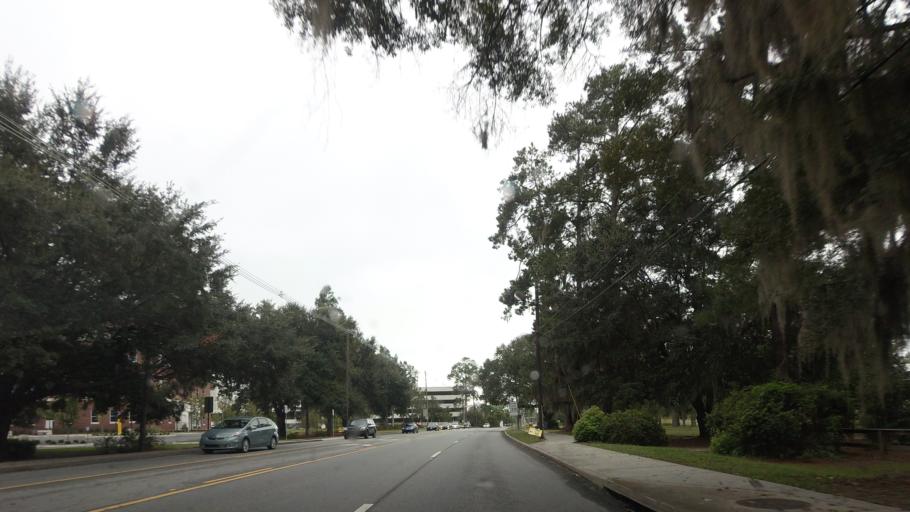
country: US
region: Georgia
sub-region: Lowndes County
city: Remerton
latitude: 30.8638
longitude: -83.2891
